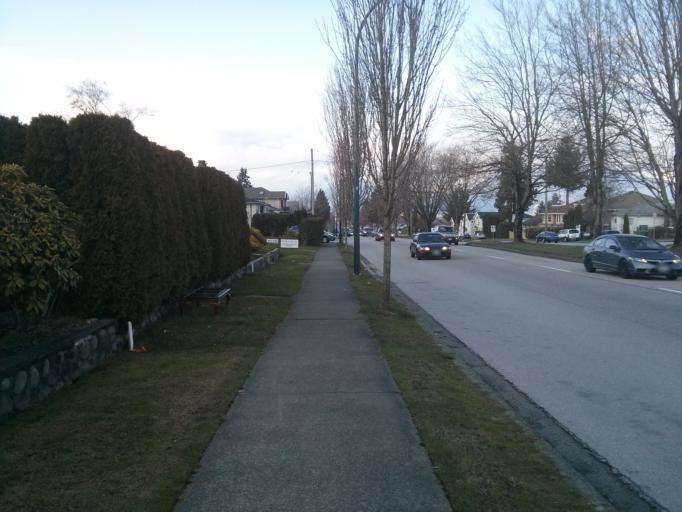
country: CA
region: British Columbia
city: Burnaby
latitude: 49.2464
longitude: -123.0239
